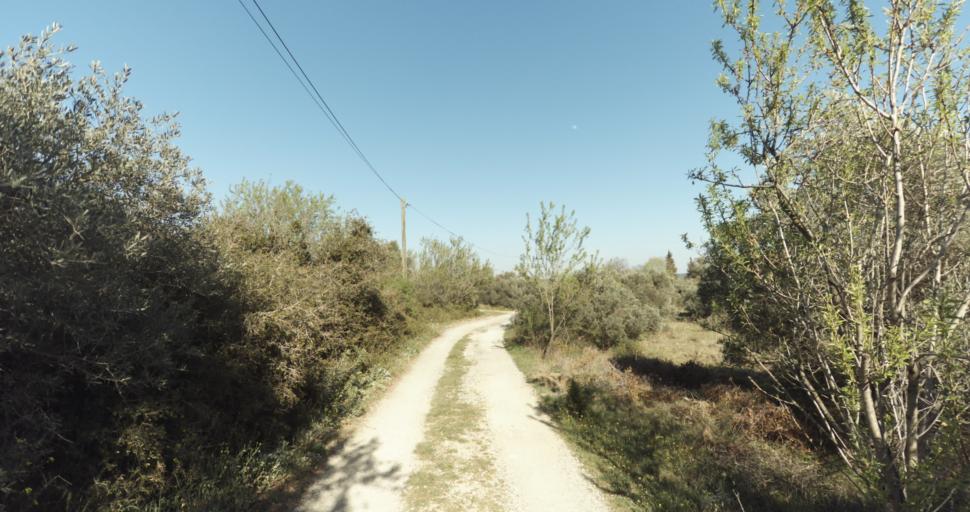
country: FR
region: Provence-Alpes-Cote d'Azur
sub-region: Departement des Bouches-du-Rhone
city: Pelissanne
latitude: 43.6355
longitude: 5.1327
